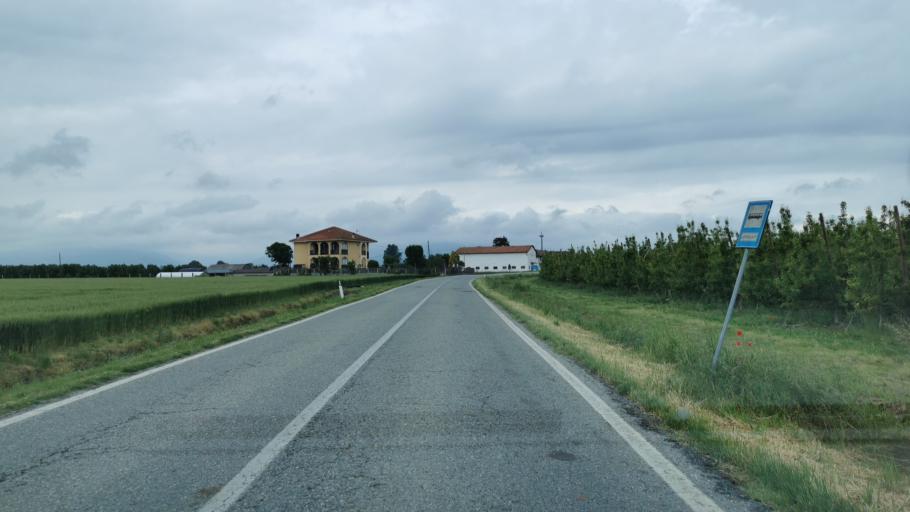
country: IT
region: Piedmont
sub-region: Provincia di Cuneo
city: Vottignasco
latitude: 44.6050
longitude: 7.5948
